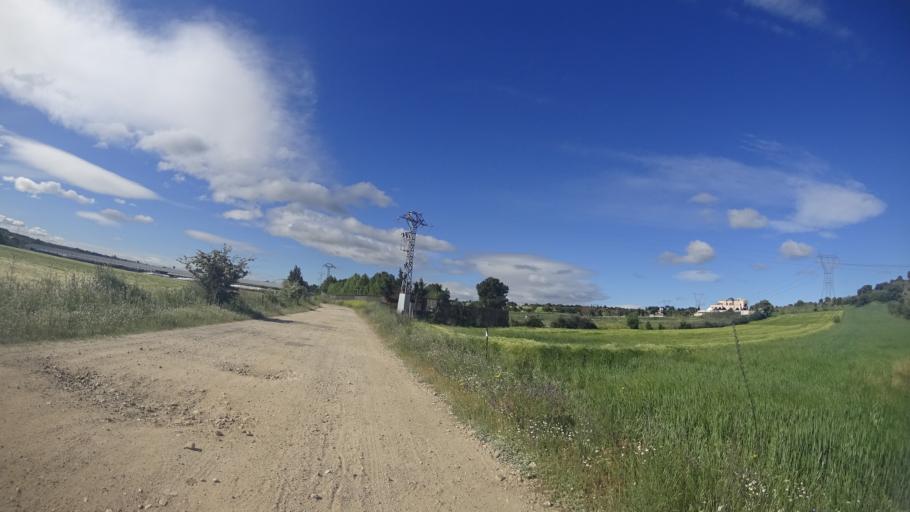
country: ES
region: Madrid
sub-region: Provincia de Madrid
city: Villanueva del Pardillo
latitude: 40.4990
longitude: -3.9403
